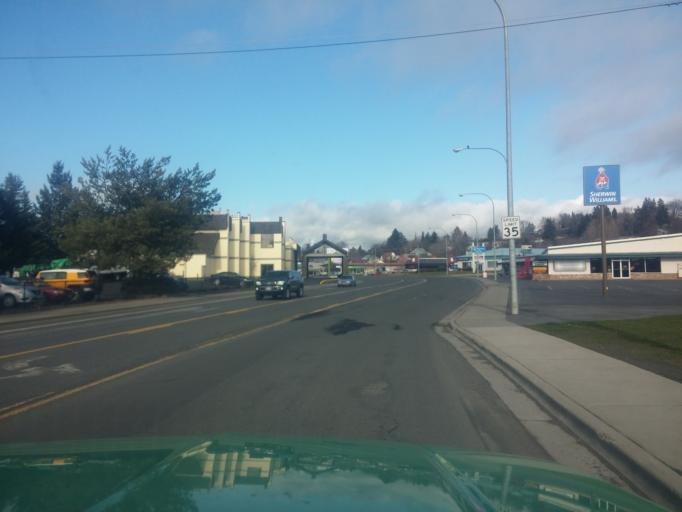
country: US
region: Idaho
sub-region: Latah County
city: Moscow
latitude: 46.7326
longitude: -117.0081
